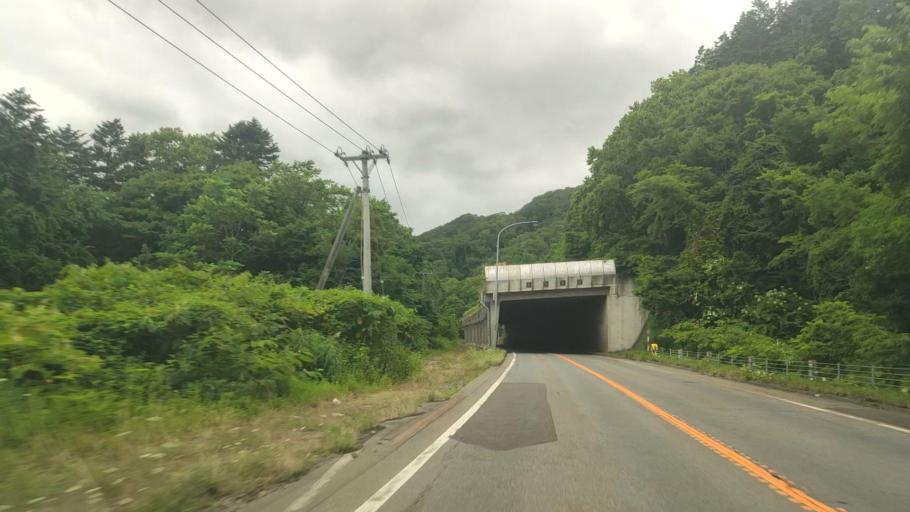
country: JP
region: Hokkaido
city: Niseko Town
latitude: 42.6023
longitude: 140.5706
